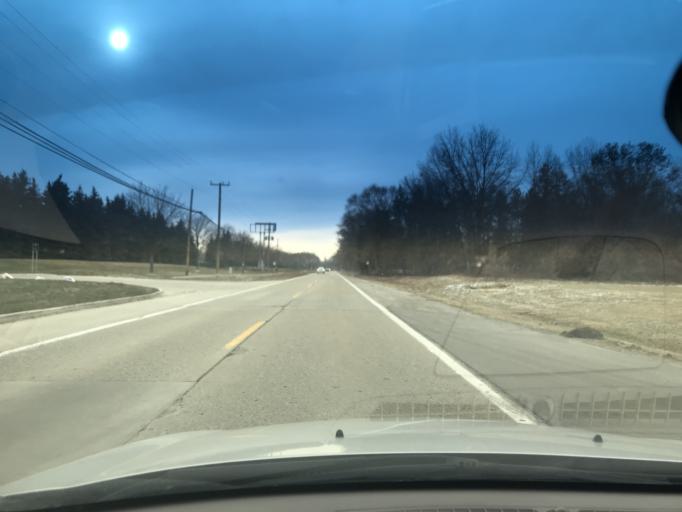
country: US
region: Michigan
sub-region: Macomb County
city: Shelby
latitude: 42.6639
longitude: -83.0534
